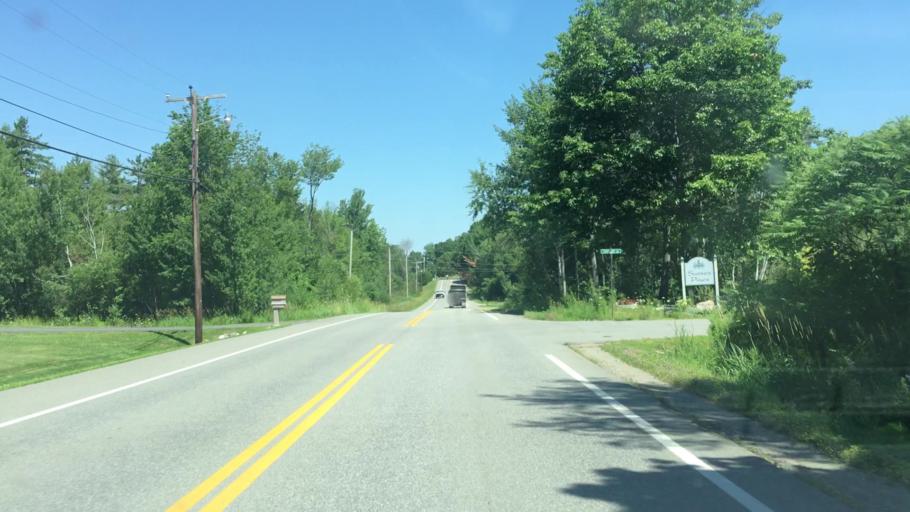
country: US
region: Maine
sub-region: Penobscot County
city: Bangor
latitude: 44.8307
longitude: -68.8133
